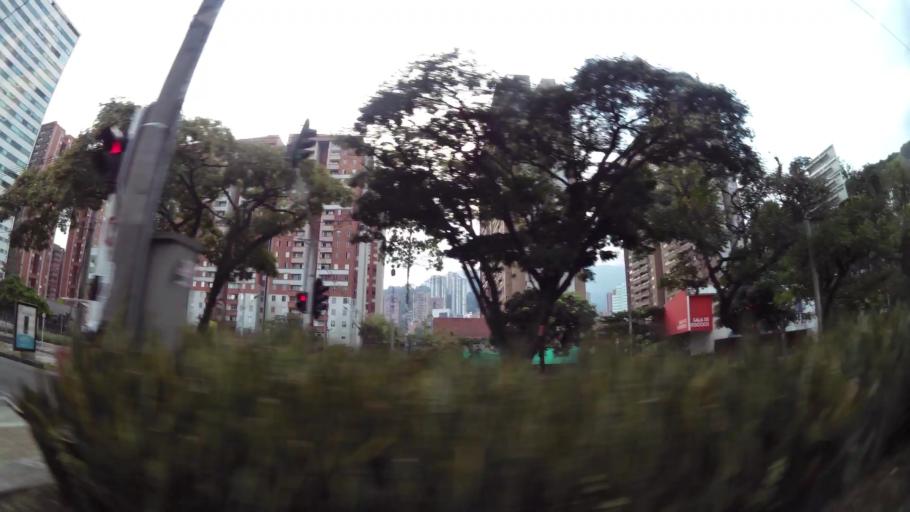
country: CO
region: Antioquia
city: Medellin
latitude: 6.2214
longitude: -75.5754
